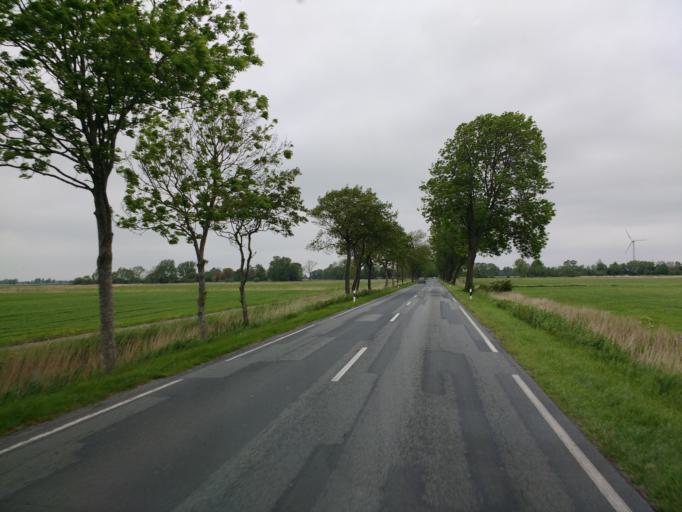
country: DE
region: Lower Saxony
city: Jever
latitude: 53.6223
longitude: 7.9296
